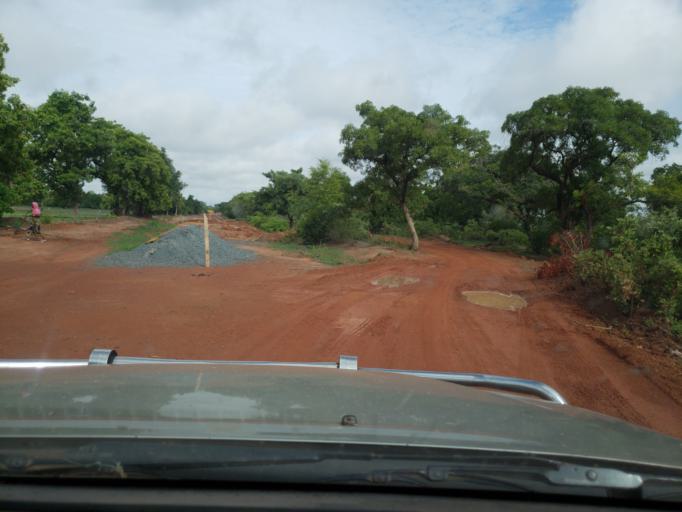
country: ML
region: Sikasso
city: Koutiala
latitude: 12.3925
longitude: -6.0155
